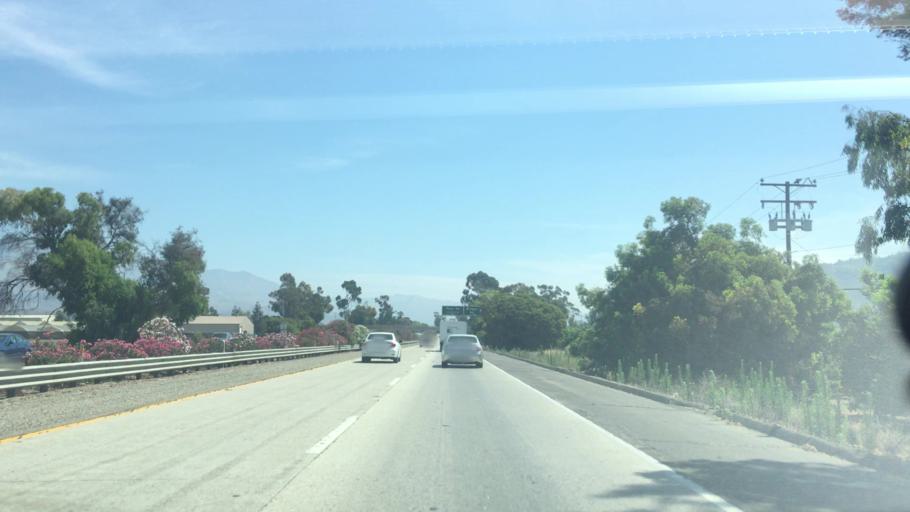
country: US
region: California
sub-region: Ventura County
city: Saticoy
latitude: 34.3195
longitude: -119.1059
